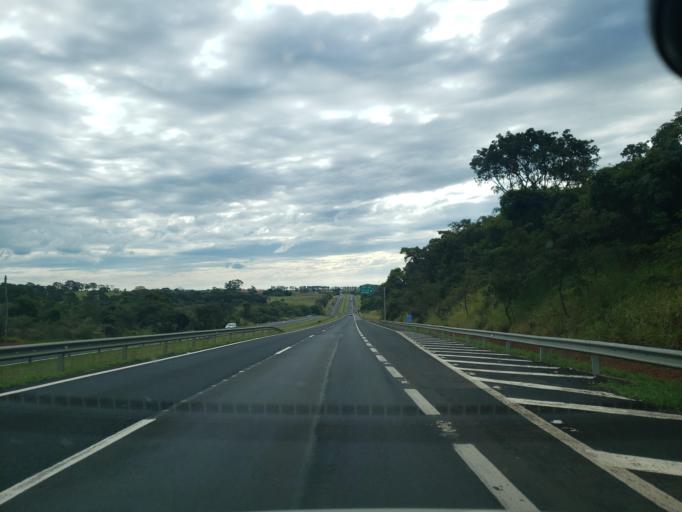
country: BR
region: Sao Paulo
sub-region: Bauru
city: Bauru
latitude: -22.2090
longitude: -49.1811
